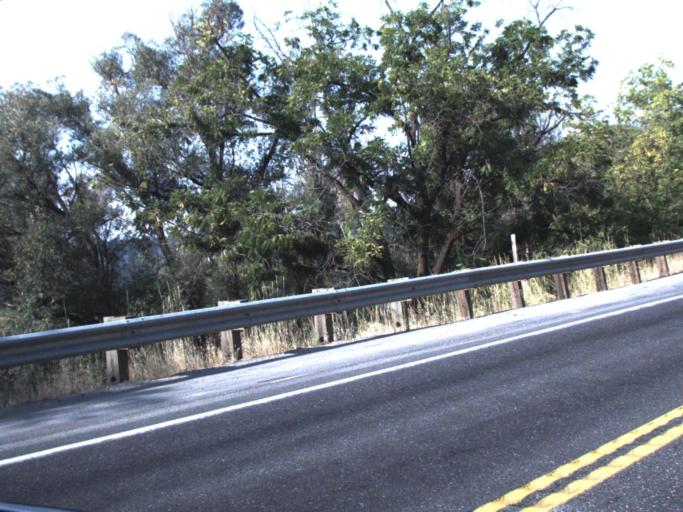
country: US
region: Washington
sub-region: Spokane County
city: Fairwood
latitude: 47.8038
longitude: -117.5517
